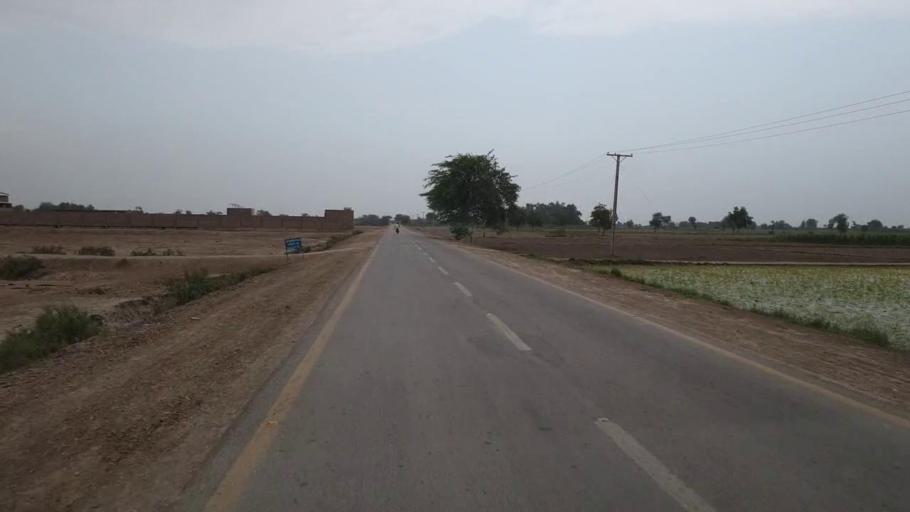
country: PK
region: Sindh
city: Bandhi
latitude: 26.5906
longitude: 68.1995
